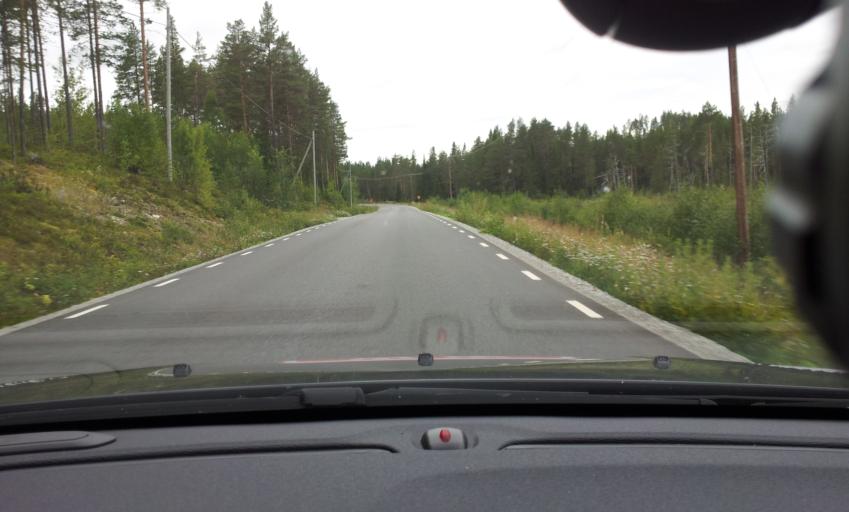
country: SE
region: Jaemtland
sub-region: Braecke Kommun
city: Braecke
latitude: 63.0691
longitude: 15.3559
